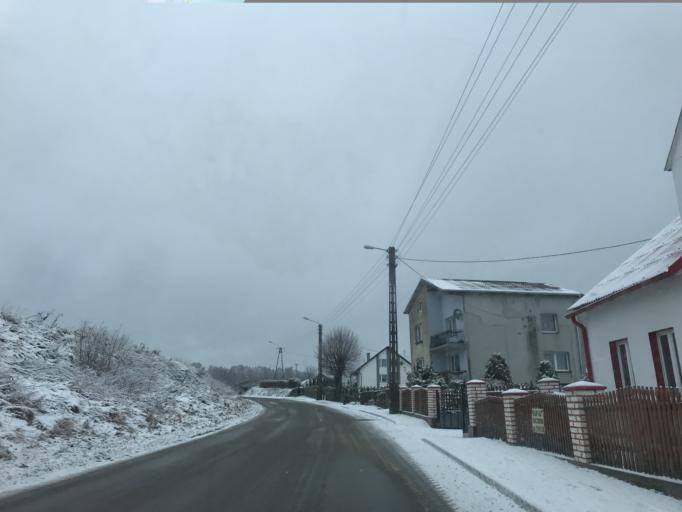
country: PL
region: Pomeranian Voivodeship
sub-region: Powiat bytowski
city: Bytow
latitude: 54.2185
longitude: 17.5624
